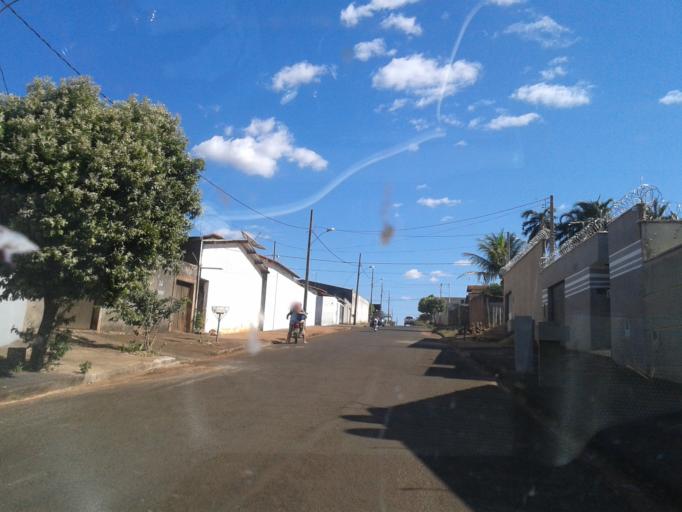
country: BR
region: Minas Gerais
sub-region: Ituiutaba
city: Ituiutaba
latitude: -18.9564
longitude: -49.4581
